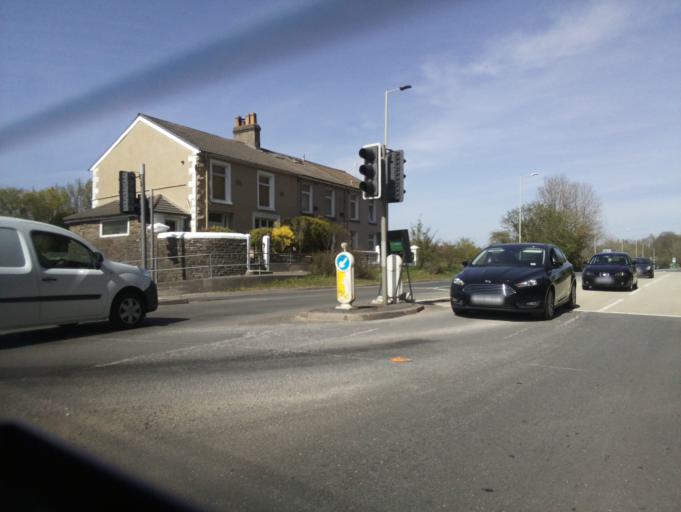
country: GB
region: Wales
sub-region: Merthyr Tydfil County Borough
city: Treharris
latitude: 51.6422
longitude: -3.3243
